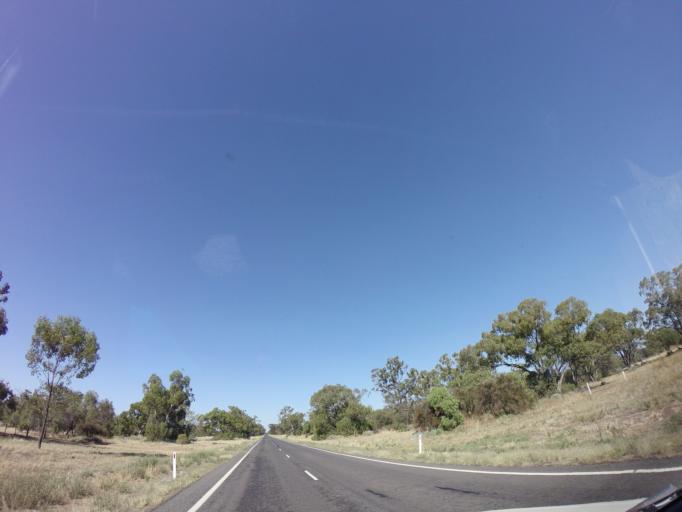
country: AU
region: New South Wales
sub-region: Narromine
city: Narromine
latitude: -31.6534
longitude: 147.8823
